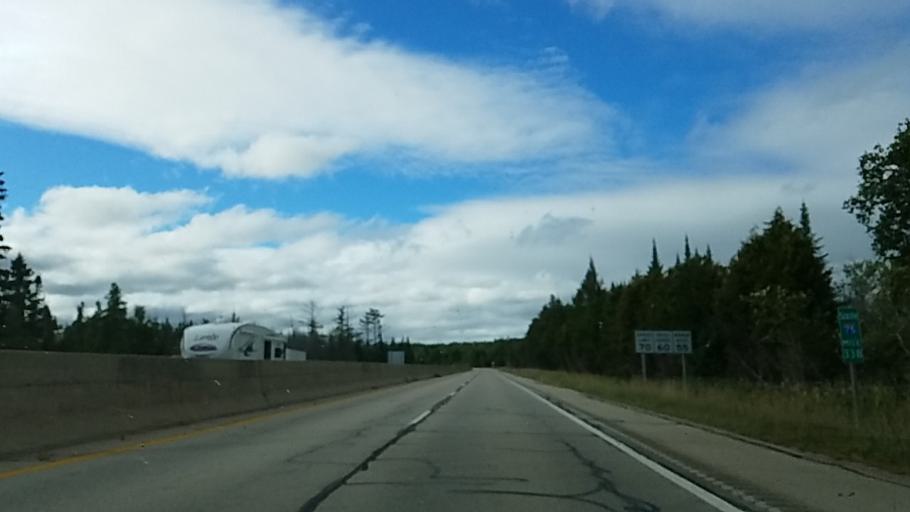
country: US
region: Michigan
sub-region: Mackinac County
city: Saint Ignace
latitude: 45.7709
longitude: -84.7348
